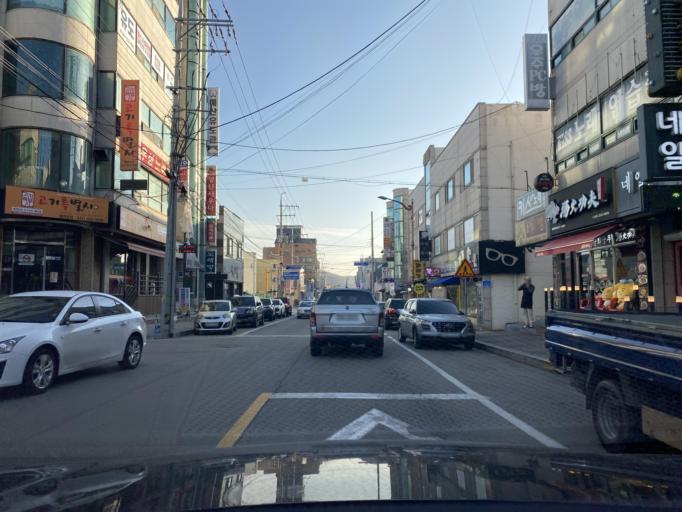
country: KR
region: Chungcheongnam-do
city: Yesan
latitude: 36.6913
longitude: 126.8301
